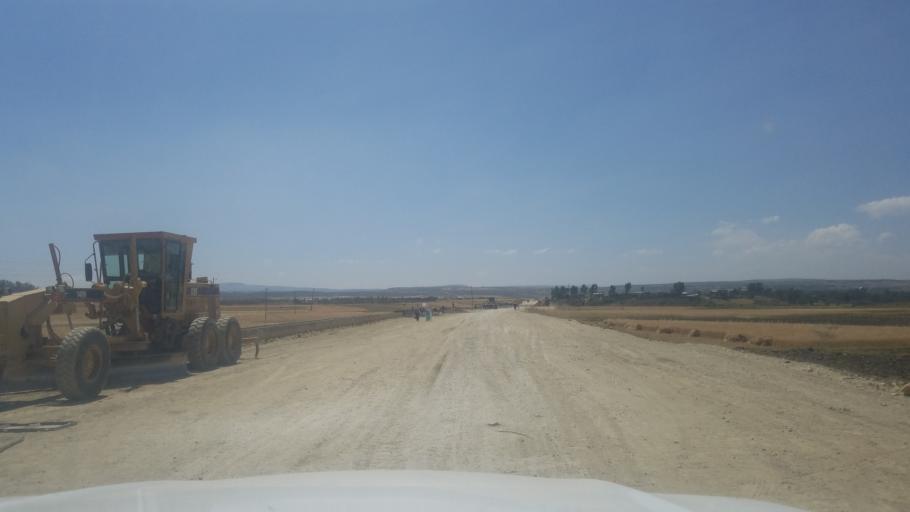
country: ET
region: Tigray
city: Mekele
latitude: 13.7672
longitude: 39.5911
